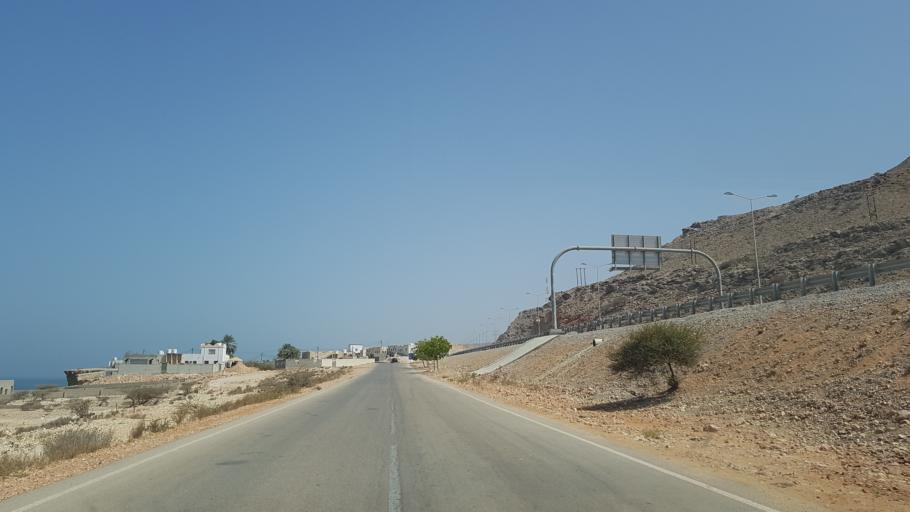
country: OM
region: Ash Sharqiyah
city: Sur
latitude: 22.8427
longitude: 59.2433
